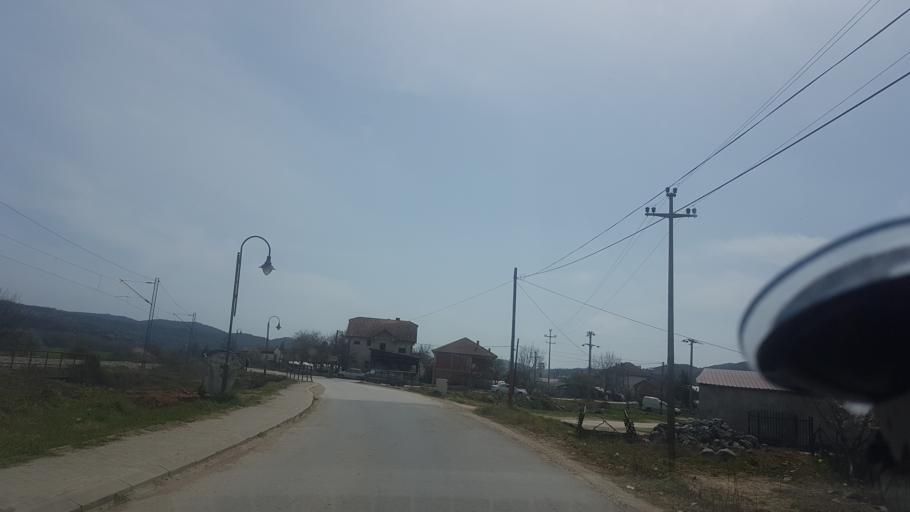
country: MK
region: Zelenikovo
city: Zelenikovo
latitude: 41.8840
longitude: 21.5892
